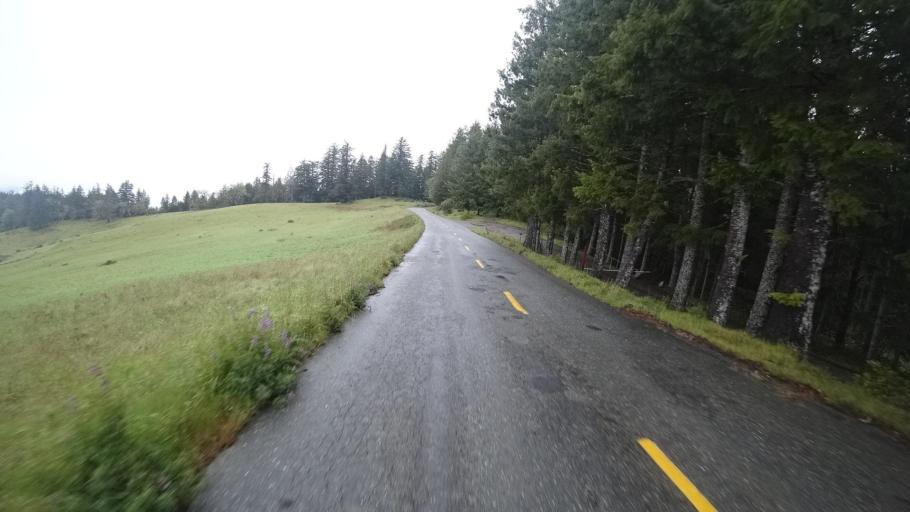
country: US
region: California
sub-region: Humboldt County
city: Westhaven-Moonstone
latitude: 41.2289
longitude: -123.9729
